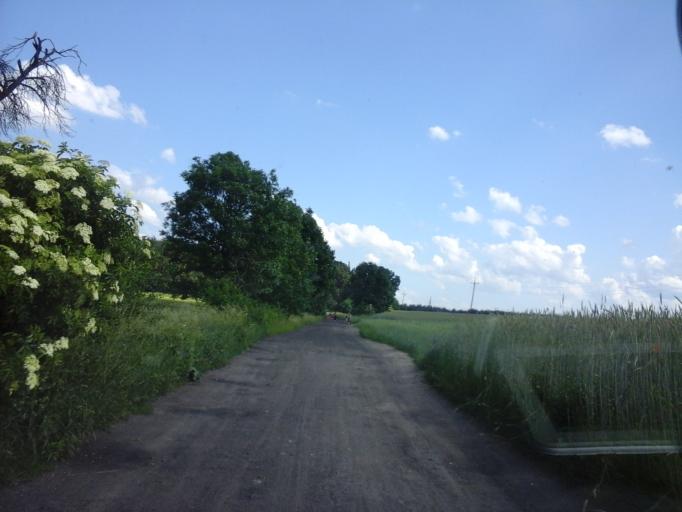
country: PL
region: Lubusz
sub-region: Powiat strzelecko-drezdenecki
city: Dobiegniew
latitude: 53.0207
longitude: 15.7433
